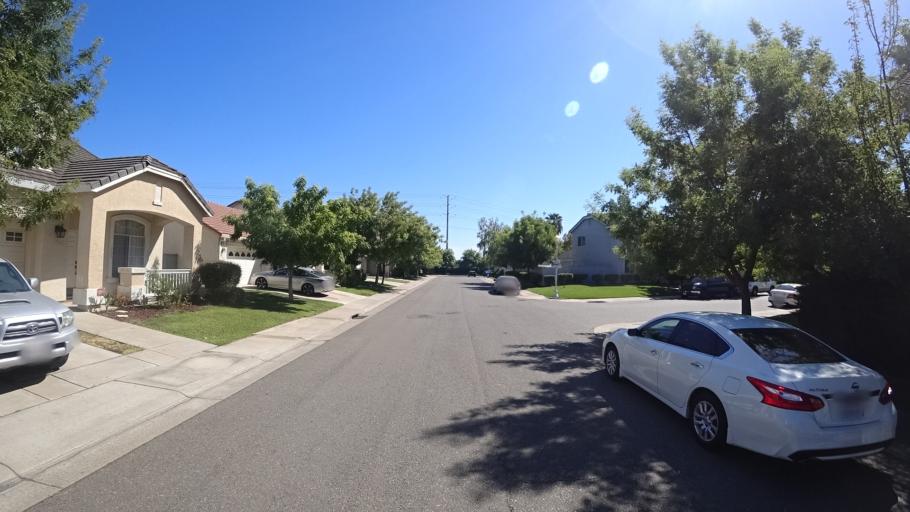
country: US
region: California
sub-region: Sacramento County
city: Laguna
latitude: 38.4234
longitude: -121.4584
